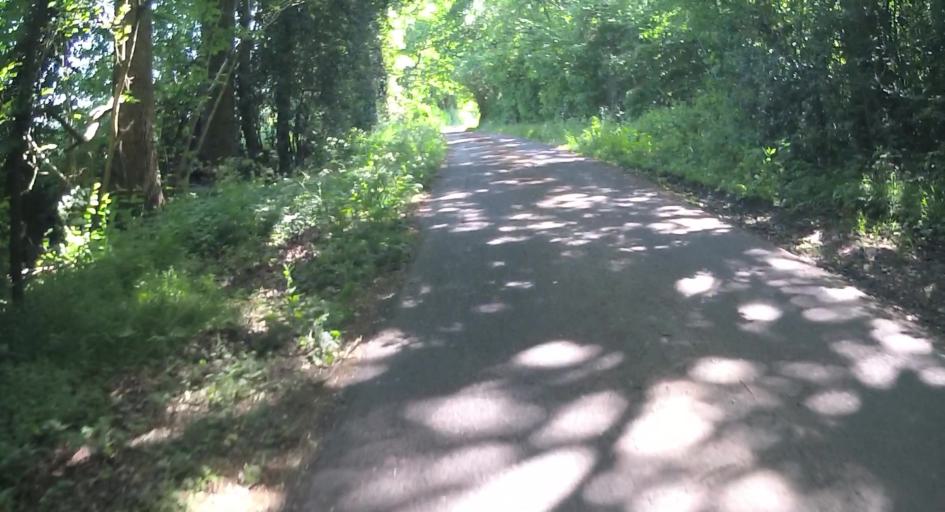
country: GB
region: England
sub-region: West Berkshire
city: Greenham
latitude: 51.3618
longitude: -1.2771
